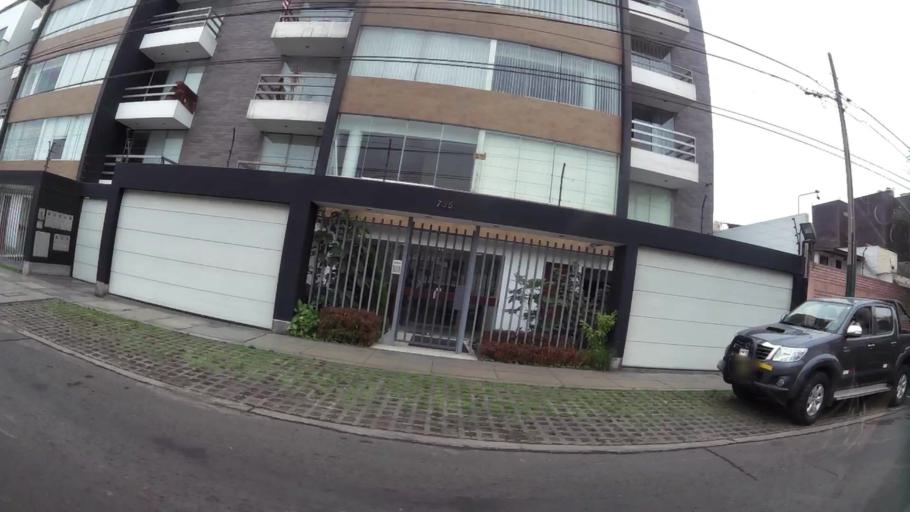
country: PE
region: Lima
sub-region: Lima
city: La Molina
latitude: -12.1113
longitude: -76.9717
